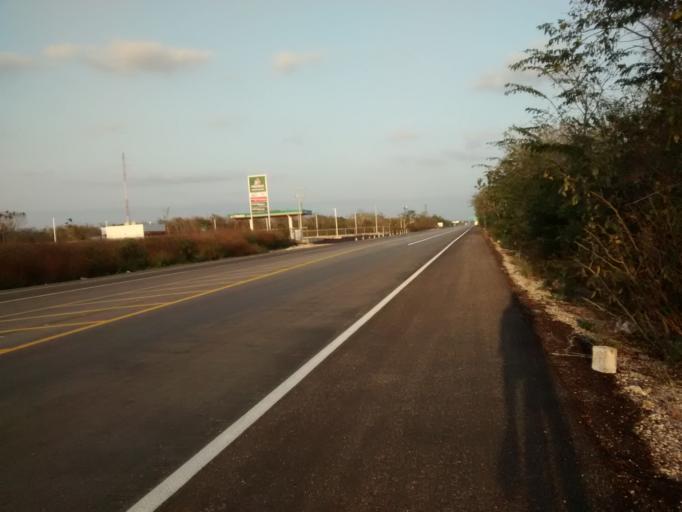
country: MX
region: Yucatan
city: Valladolid
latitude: 20.7251
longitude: -88.2118
